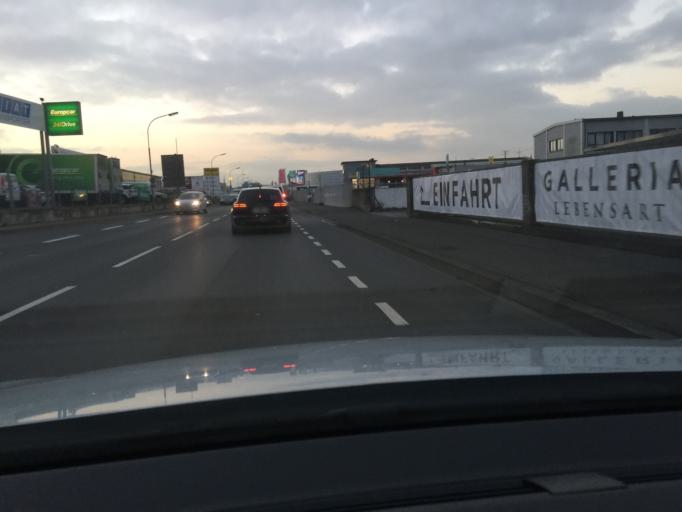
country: DE
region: Rheinland-Pfalz
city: Koblenz
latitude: 50.3775
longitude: 7.5876
